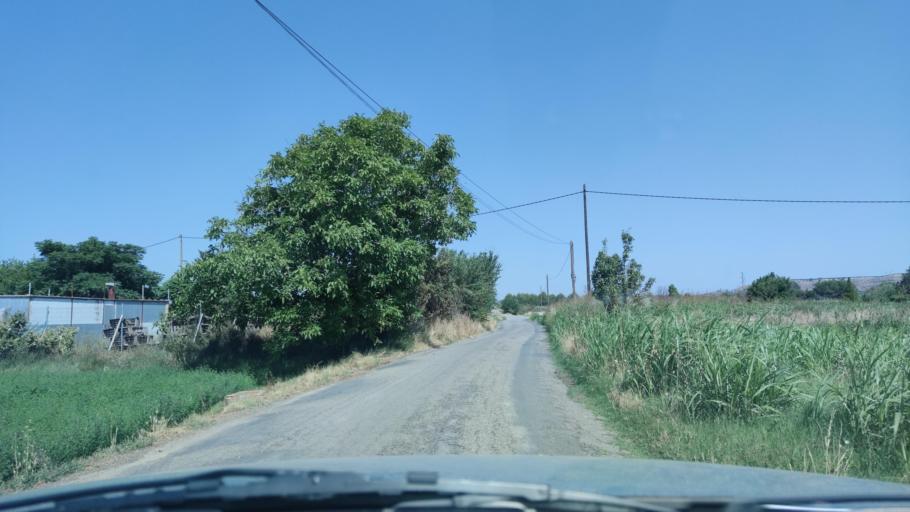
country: ES
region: Catalonia
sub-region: Provincia de Lleida
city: Alpicat
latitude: 41.6508
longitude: 0.5793
